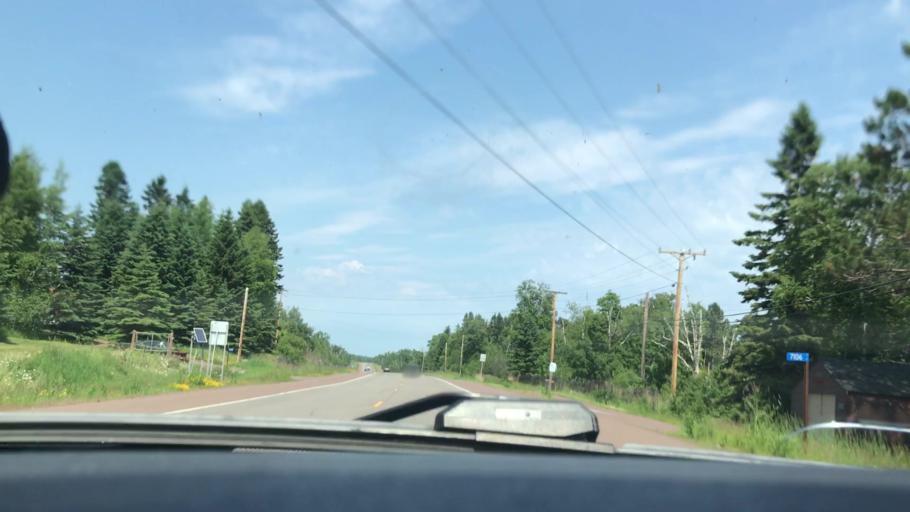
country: US
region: Minnesota
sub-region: Lake County
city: Silver Bay
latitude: 47.5779
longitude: -90.8282
